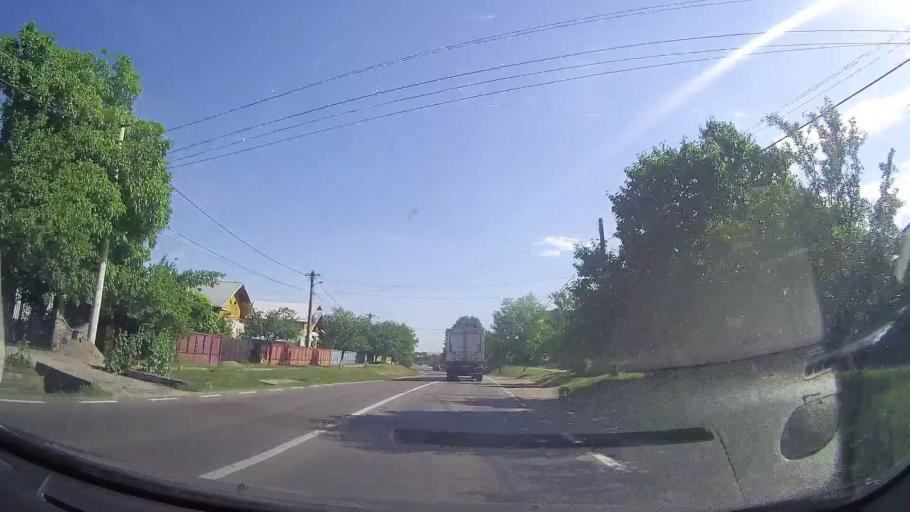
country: RO
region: Prahova
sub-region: Comuna Magurele
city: Magurele
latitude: 45.1080
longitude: 26.0356
